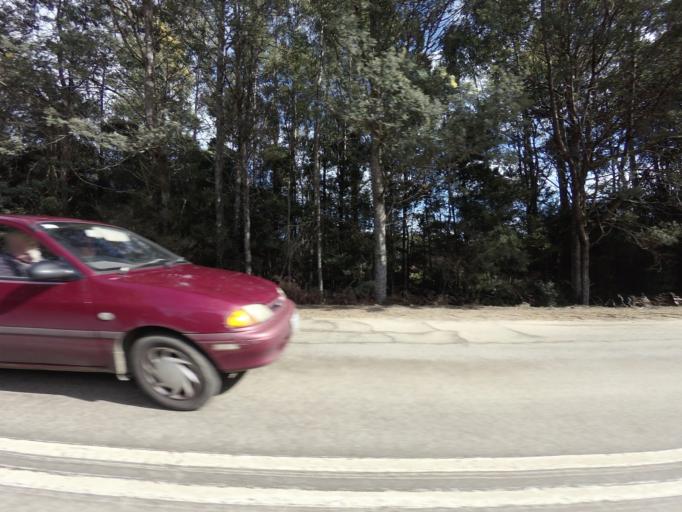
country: AU
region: Tasmania
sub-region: Huon Valley
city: Geeveston
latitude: -43.3503
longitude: 146.9571
